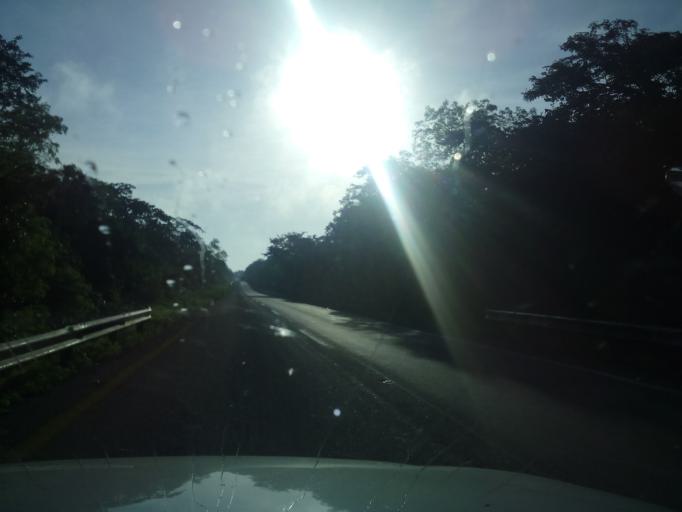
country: MX
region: Yucatan
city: Piste
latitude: 20.7457
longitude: -88.6944
